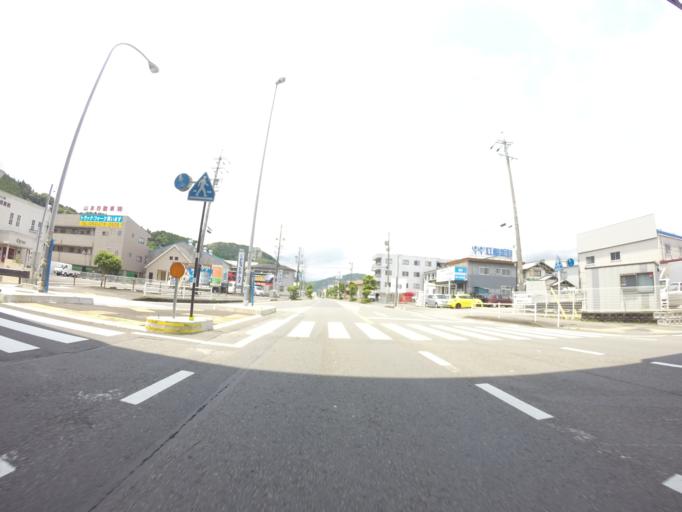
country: JP
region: Shizuoka
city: Shizuoka-shi
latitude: 34.9730
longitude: 138.3452
